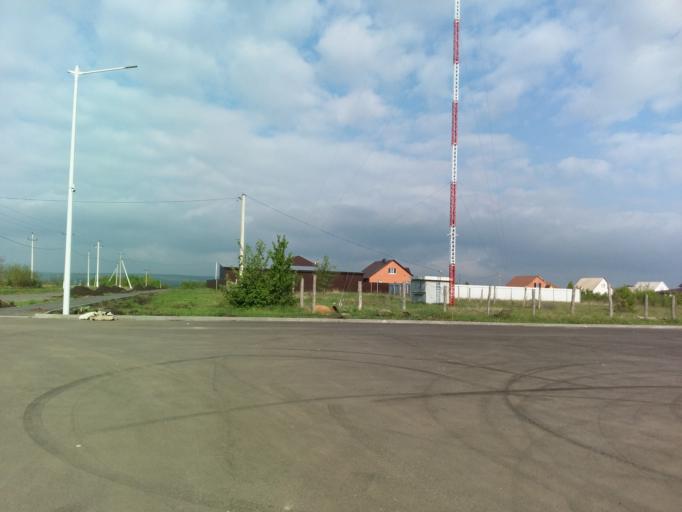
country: RU
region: Voronezj
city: Kalach
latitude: 50.4154
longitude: 41.0007
